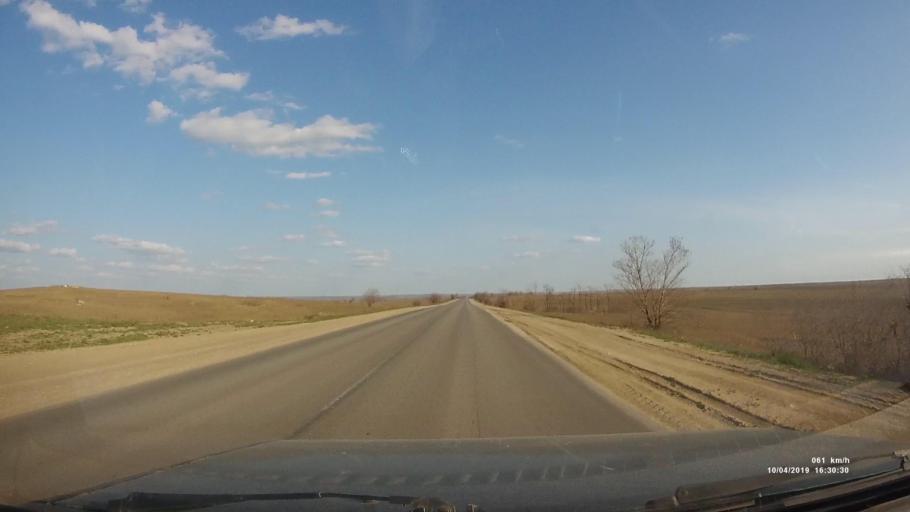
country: RU
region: Rostov
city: Staraya Stanitsa
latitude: 48.2616
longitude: 40.3659
